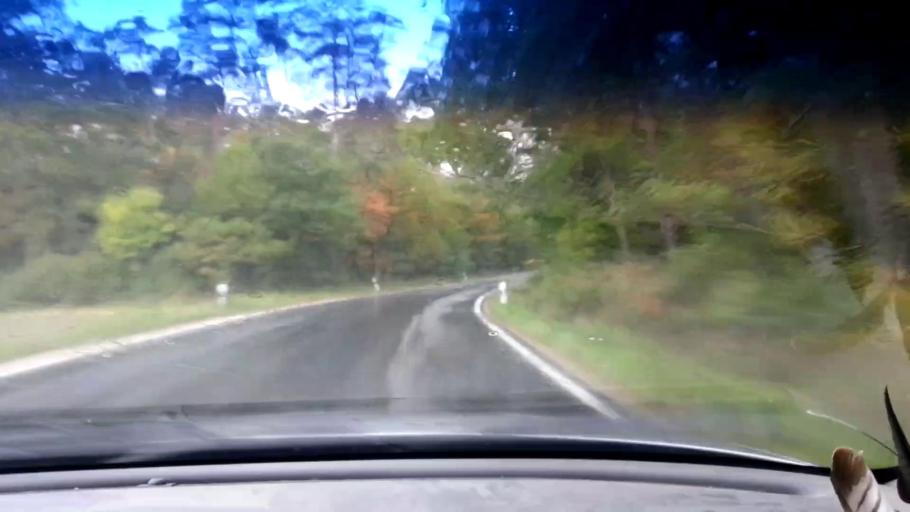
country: DE
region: Bavaria
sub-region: Upper Franconia
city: Walsdorf
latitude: 49.8677
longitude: 10.7655
